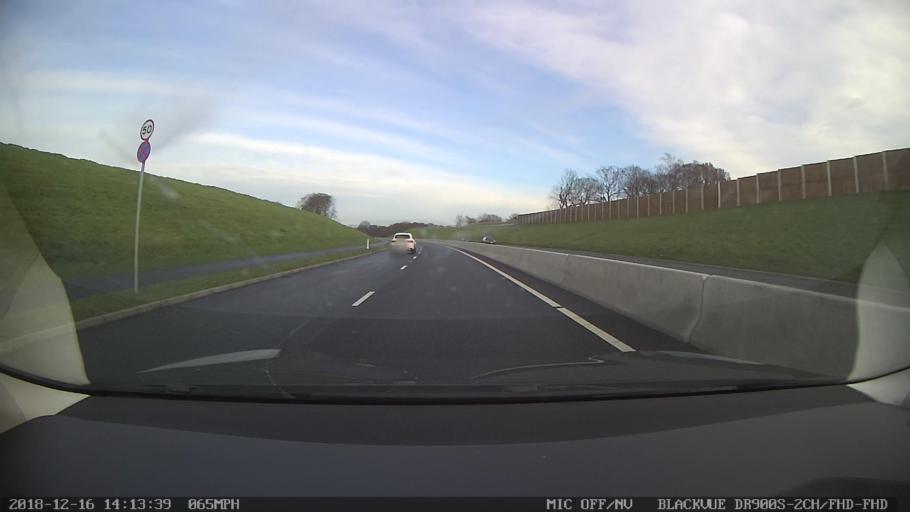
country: GB
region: England
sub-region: Cheshire East
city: Poynton
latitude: 53.3593
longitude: -2.1273
